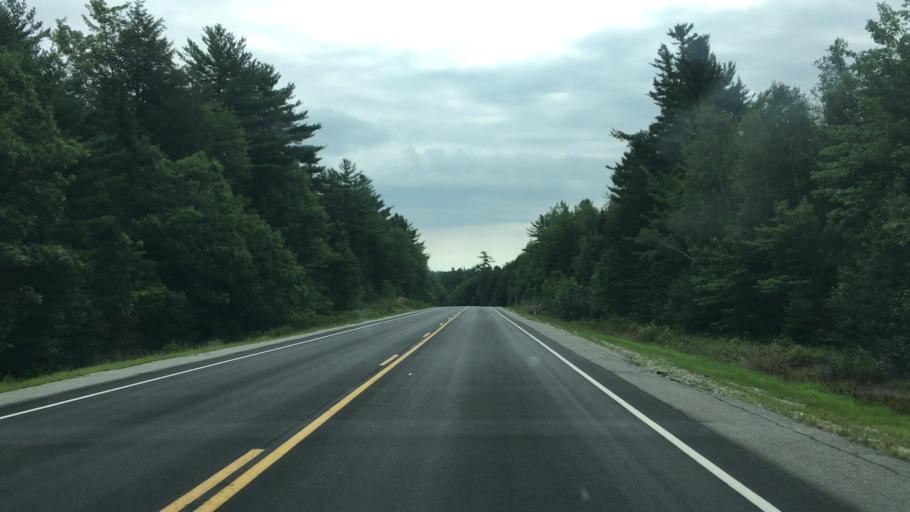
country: US
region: Maine
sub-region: Washington County
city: Addison
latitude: 44.9094
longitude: -67.8468
